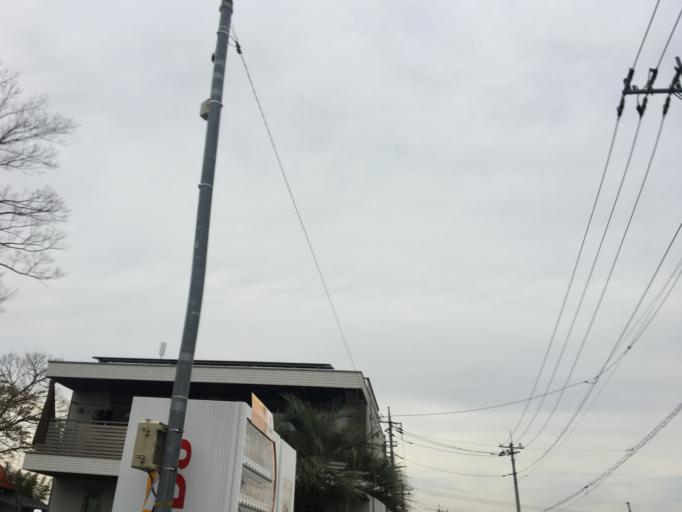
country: JP
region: Saitama
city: Shiki
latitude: 35.8611
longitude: 139.5662
